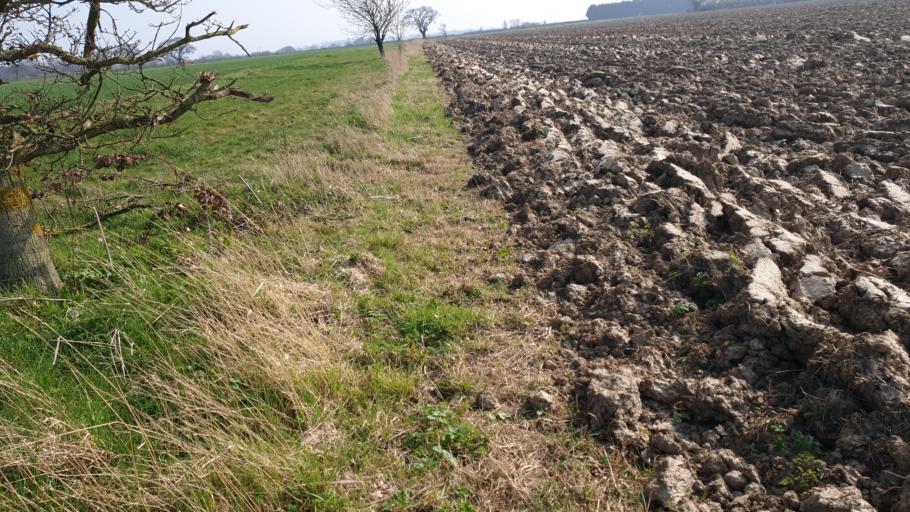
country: GB
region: England
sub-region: Essex
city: Mistley
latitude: 51.9053
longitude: 1.1279
